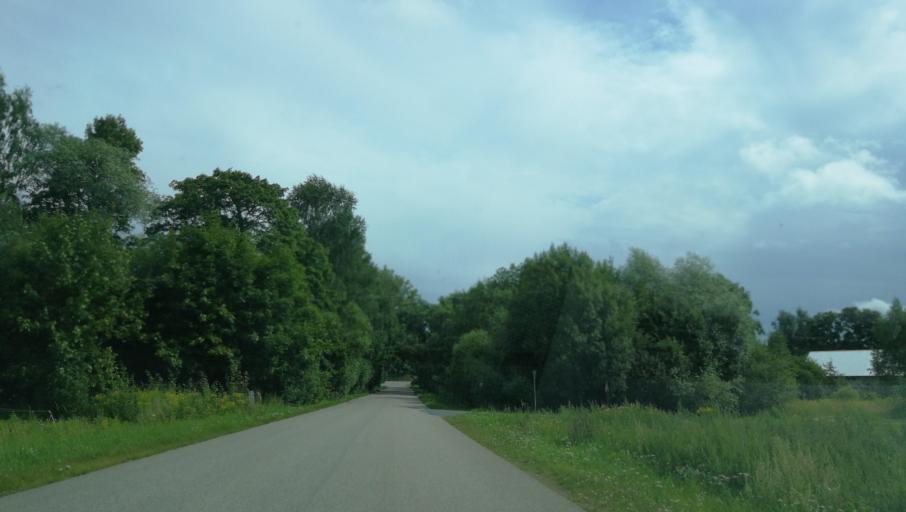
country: LV
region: Cesu Rajons
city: Cesis
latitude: 57.3272
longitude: 25.2910
